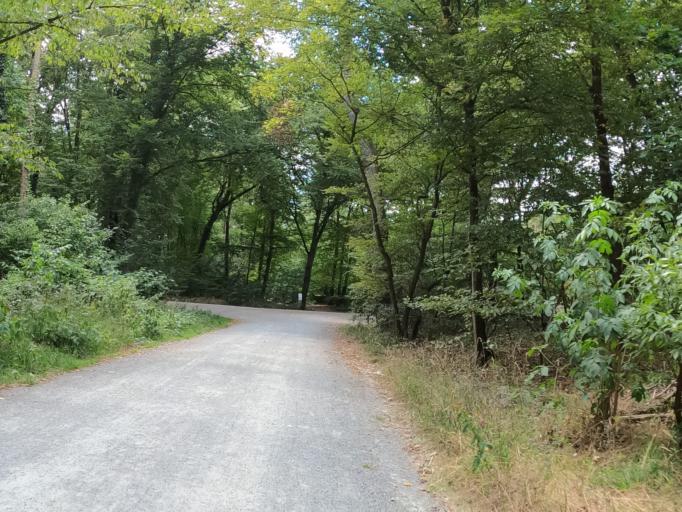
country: DE
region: Hesse
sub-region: Regierungsbezirk Darmstadt
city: Nauheim
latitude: 49.9603
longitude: 8.4621
